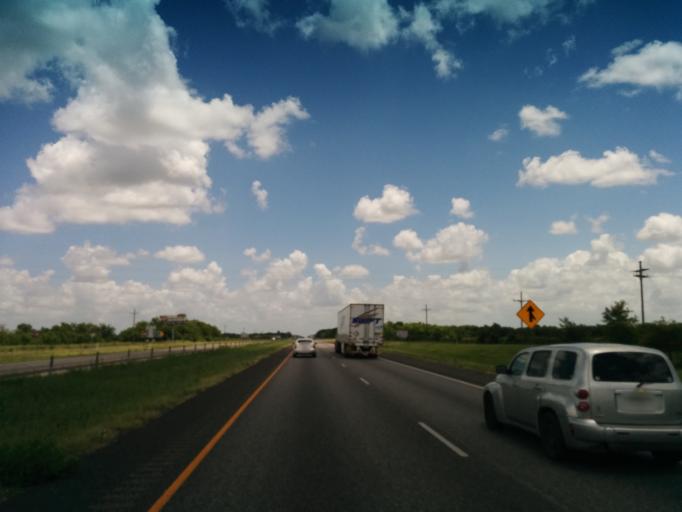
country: US
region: Texas
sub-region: Chambers County
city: Winnie
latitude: 29.8798
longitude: -94.3321
